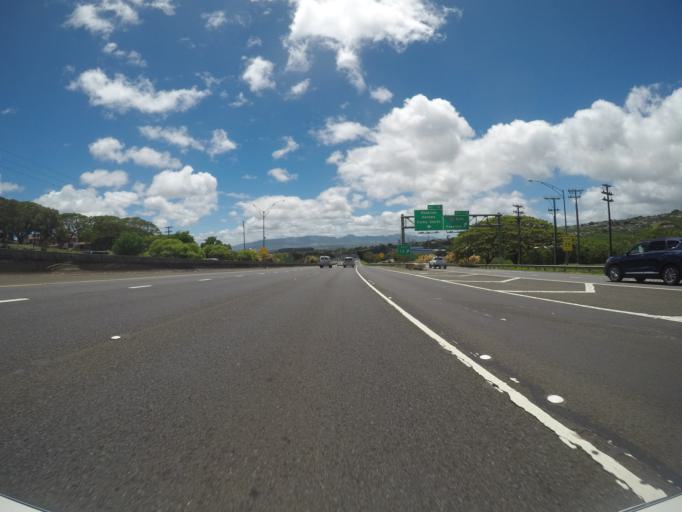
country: US
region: Hawaii
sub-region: Honolulu County
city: Halawa Heights
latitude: 21.3690
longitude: -157.9107
